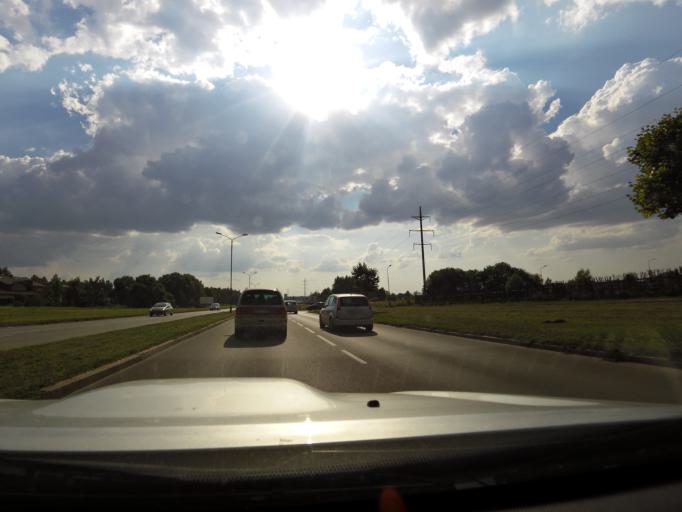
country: LT
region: Siauliu apskritis
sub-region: Siauliai
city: Siauliai
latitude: 55.9234
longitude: 23.2725
